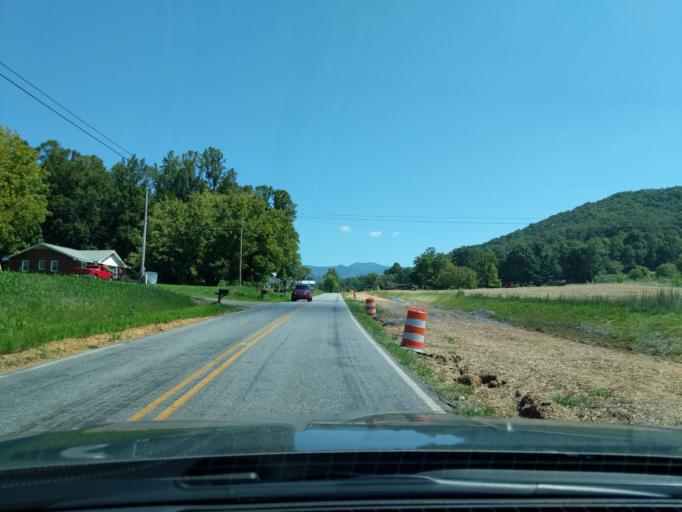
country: US
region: Georgia
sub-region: Towns County
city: Hiawassee
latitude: 35.0003
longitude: -83.7546
